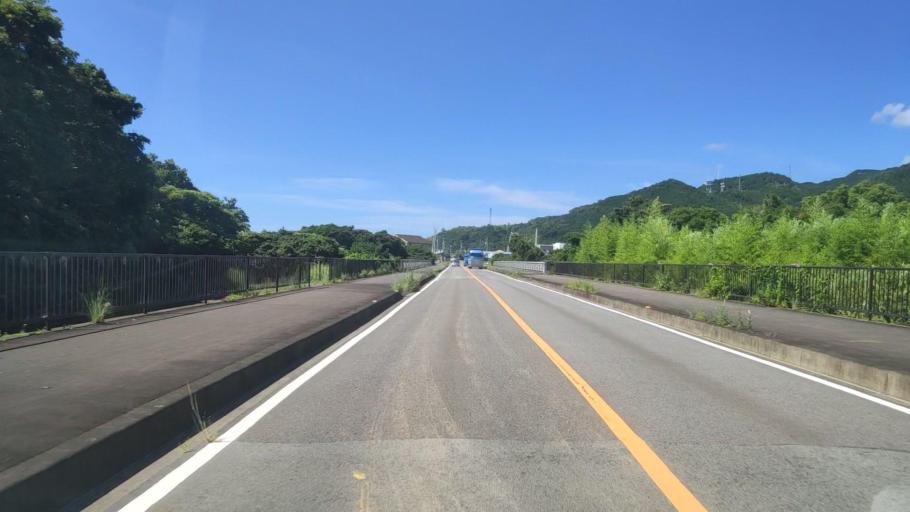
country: JP
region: Wakayama
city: Shingu
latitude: 33.7079
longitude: 135.9951
